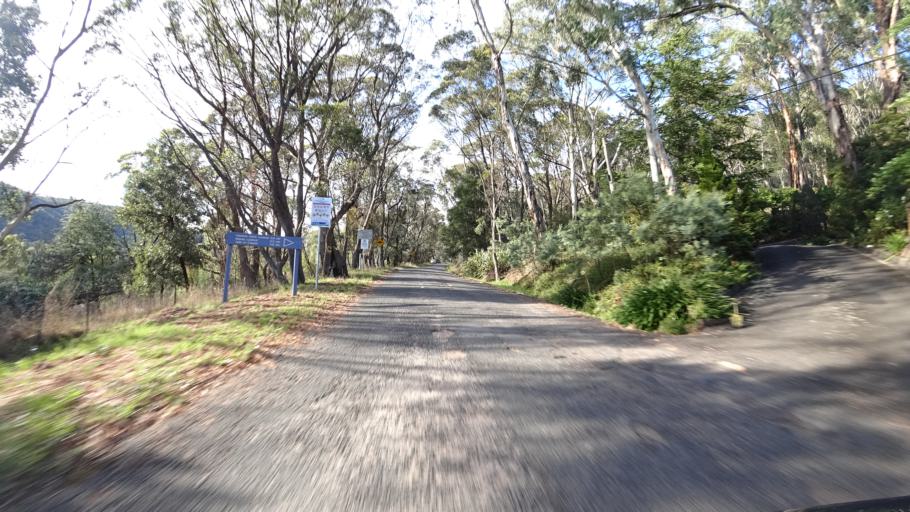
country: AU
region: New South Wales
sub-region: Lithgow
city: Lithgow
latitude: -33.4940
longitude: 150.1499
